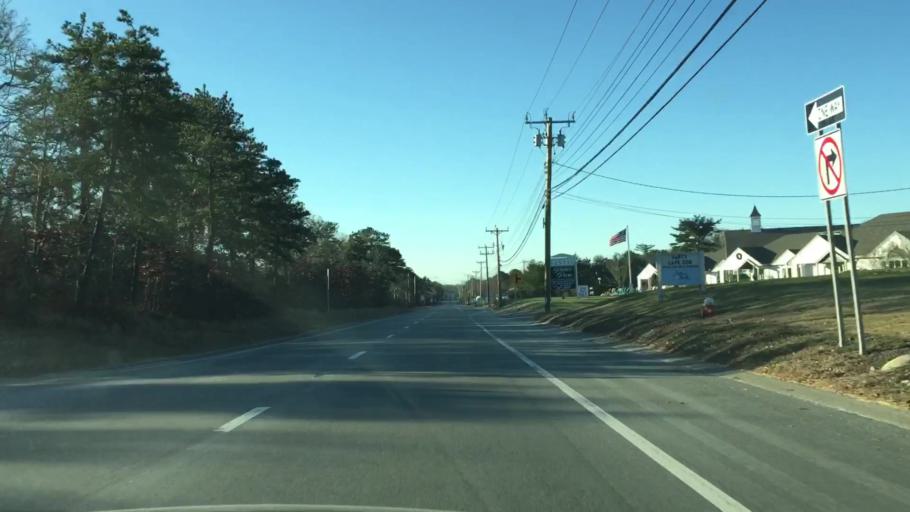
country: US
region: Massachusetts
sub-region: Barnstable County
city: Pocasset
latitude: 41.6979
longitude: -70.5856
